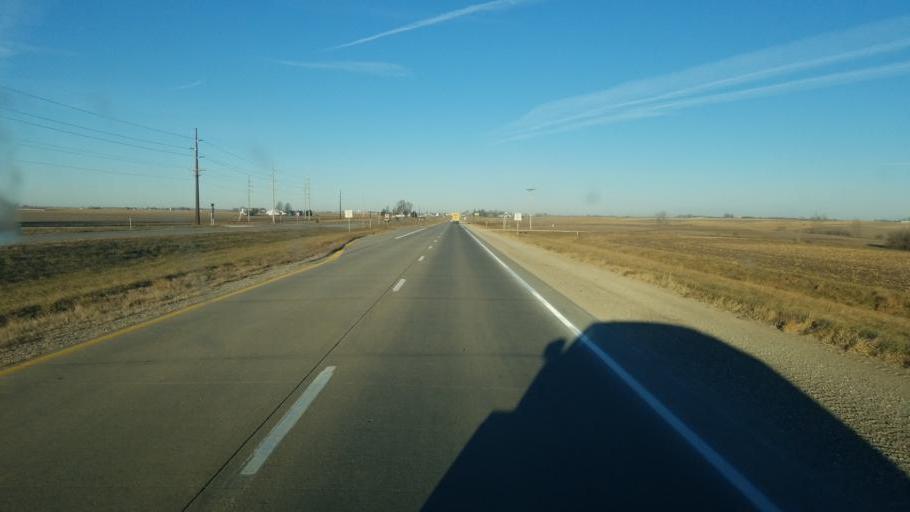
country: US
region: Iowa
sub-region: Mahaska County
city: Oskaloosa
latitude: 41.3593
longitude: -92.7737
